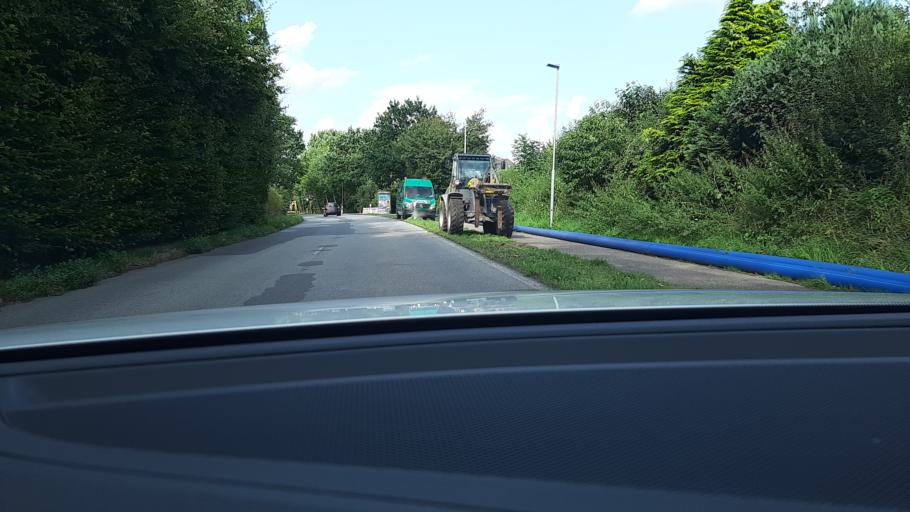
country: DE
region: Schleswig-Holstein
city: Heidekamp
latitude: 53.8408
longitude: 10.4983
